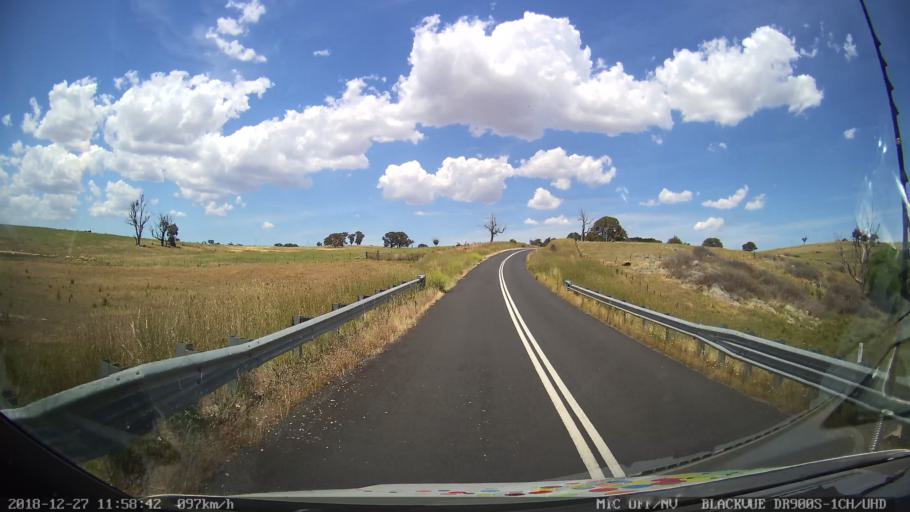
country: AU
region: New South Wales
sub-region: Blayney
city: Blayney
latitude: -33.7273
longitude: 149.3833
